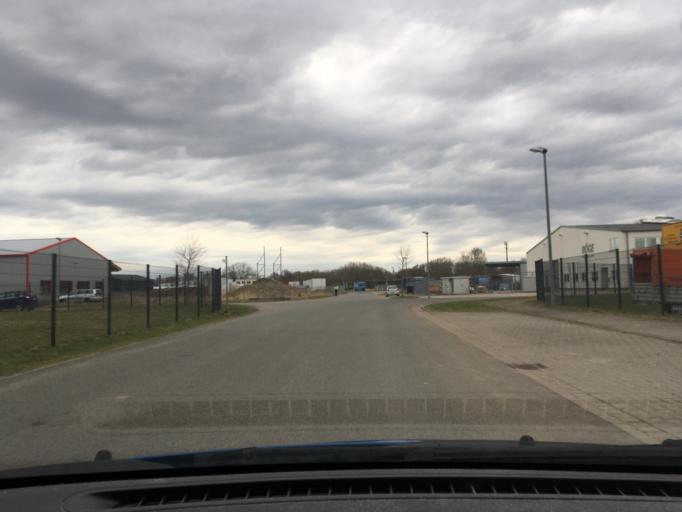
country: DE
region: Lower Saxony
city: Handorf
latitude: 53.3805
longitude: 10.3439
